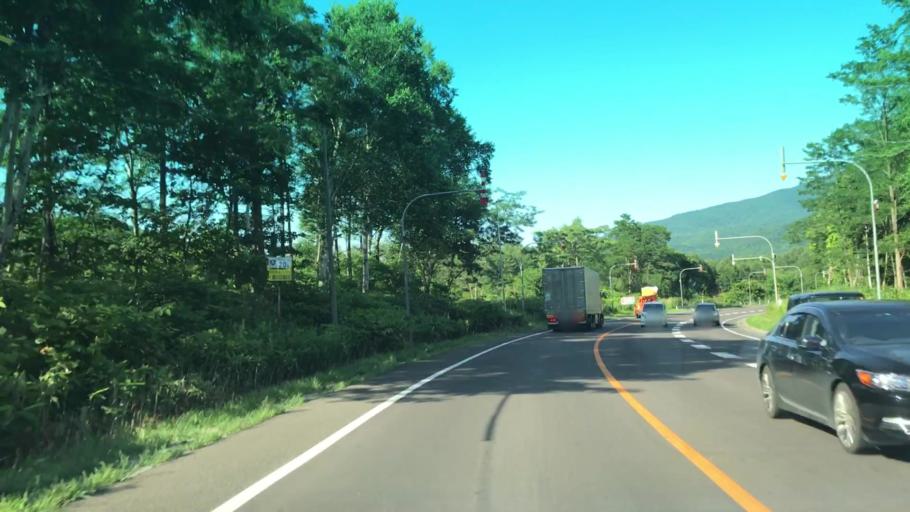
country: JP
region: Hokkaido
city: Yoichi
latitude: 43.0724
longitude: 140.6997
